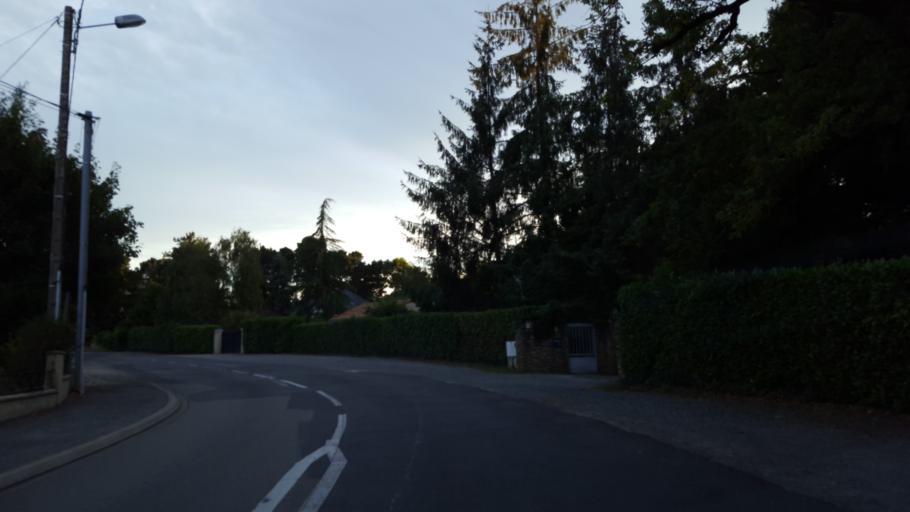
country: FR
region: Pays de la Loire
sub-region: Departement de la Loire-Atlantique
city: Basse-Goulaine
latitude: 47.2120
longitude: -1.4751
